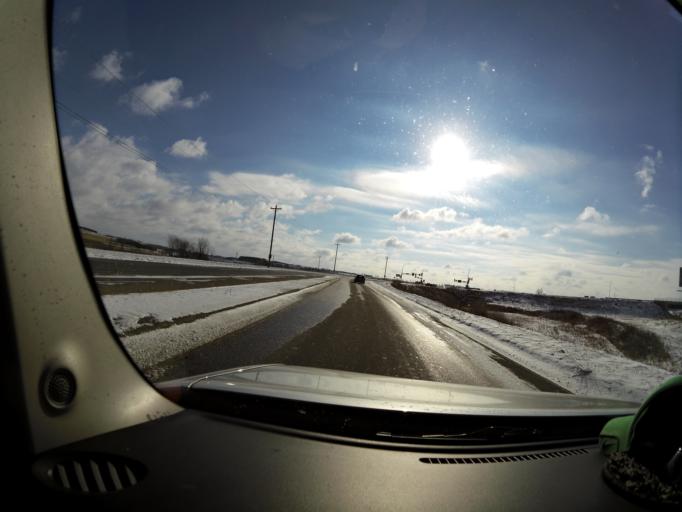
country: US
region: Minnesota
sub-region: Olmsted County
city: Rochester
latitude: 43.9656
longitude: -92.4624
